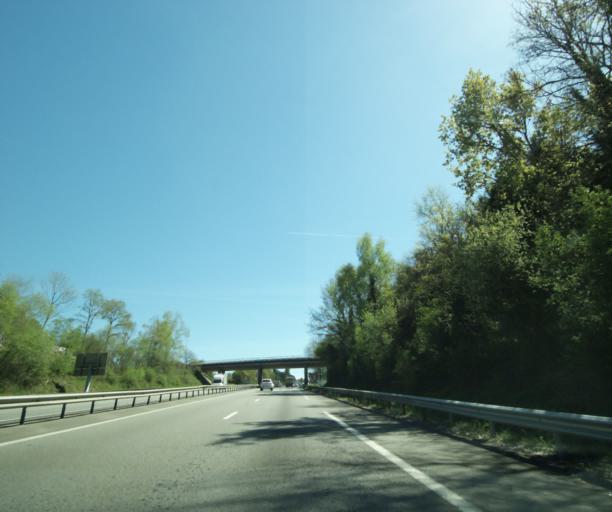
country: FR
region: Limousin
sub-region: Departement de la Haute-Vienne
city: Condat-sur-Vienne
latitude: 45.7956
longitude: 1.2987
